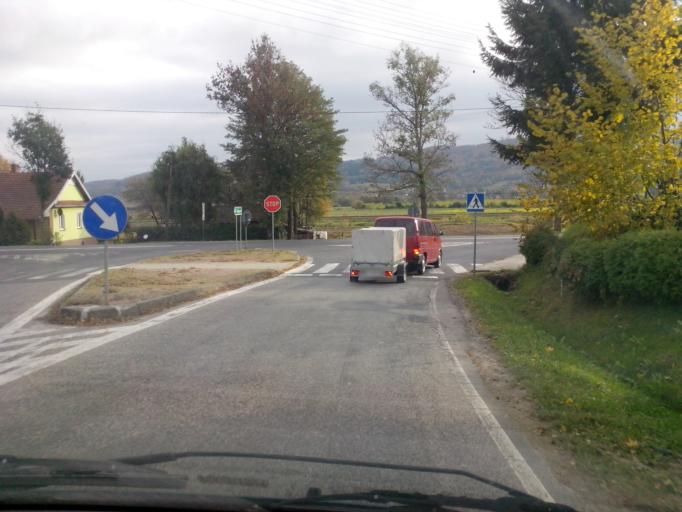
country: PL
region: Subcarpathian Voivodeship
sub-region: Powiat strzyzowski
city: Wisniowa
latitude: 49.8693
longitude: 21.6600
